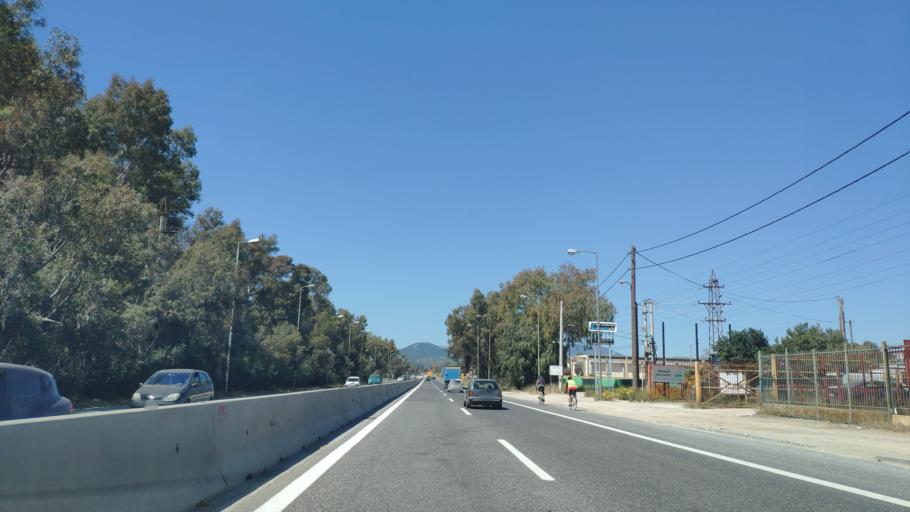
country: GR
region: Attica
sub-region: Nomarchia Dytikis Attikis
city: Aspropyrgos
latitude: 38.0498
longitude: 23.5671
